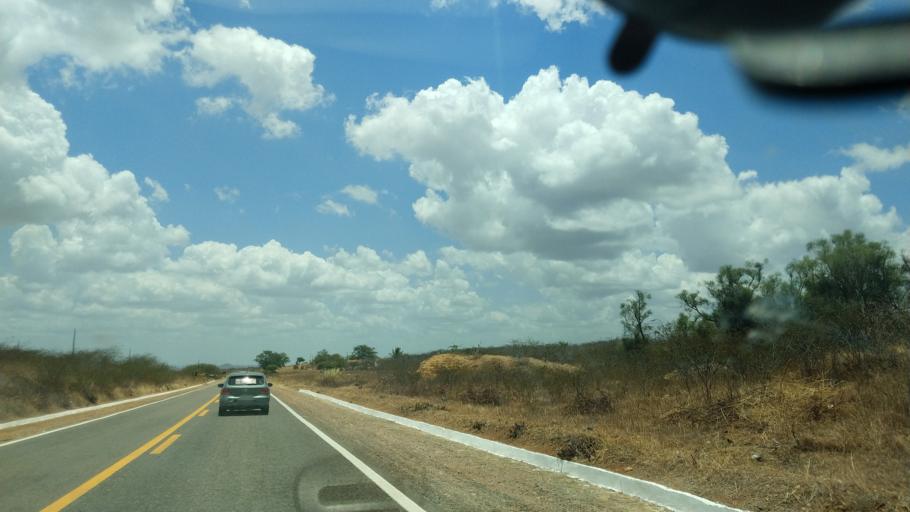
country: BR
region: Rio Grande do Norte
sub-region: Cerro Cora
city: Cerro Cora
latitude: -6.1886
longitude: -36.2459
